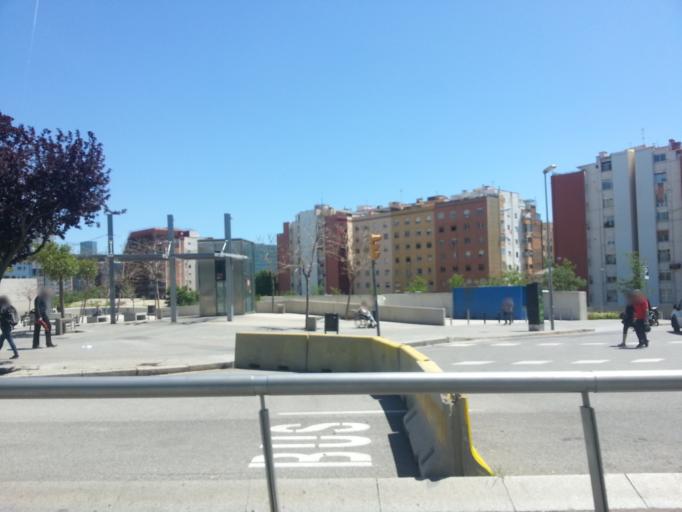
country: ES
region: Catalonia
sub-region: Provincia de Barcelona
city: Sant Marti
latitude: 41.4015
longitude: 2.1869
